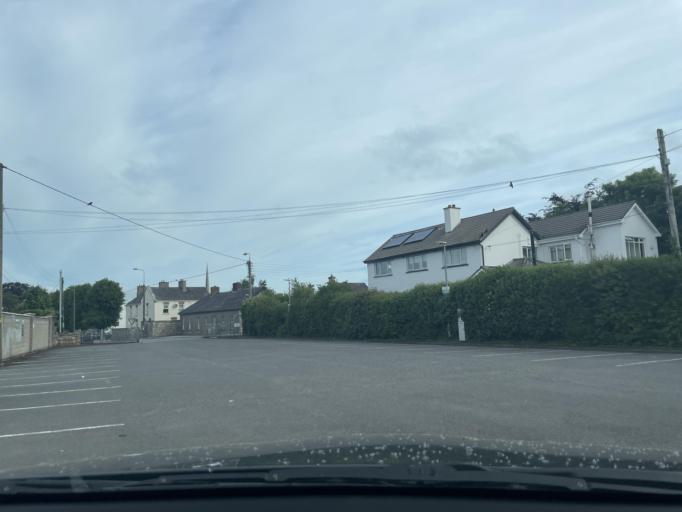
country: IE
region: Leinster
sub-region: County Carlow
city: Bagenalstown
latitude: 52.6992
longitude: -6.9528
